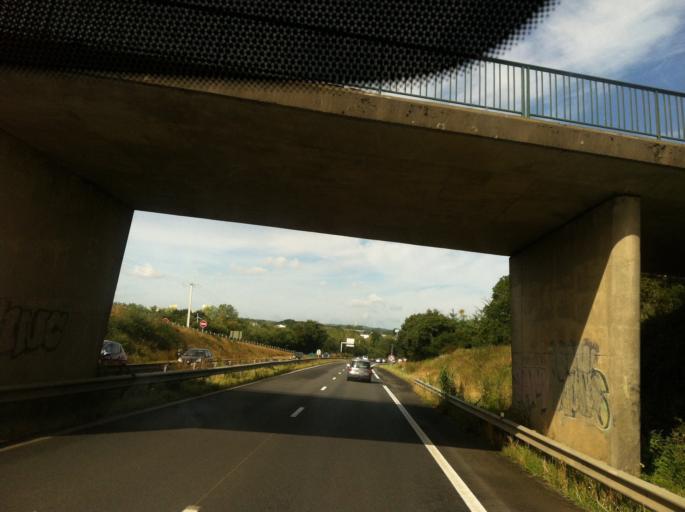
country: FR
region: Brittany
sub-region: Departement des Cotes-d'Armor
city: Guingamp
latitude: 48.5495
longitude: -3.1472
